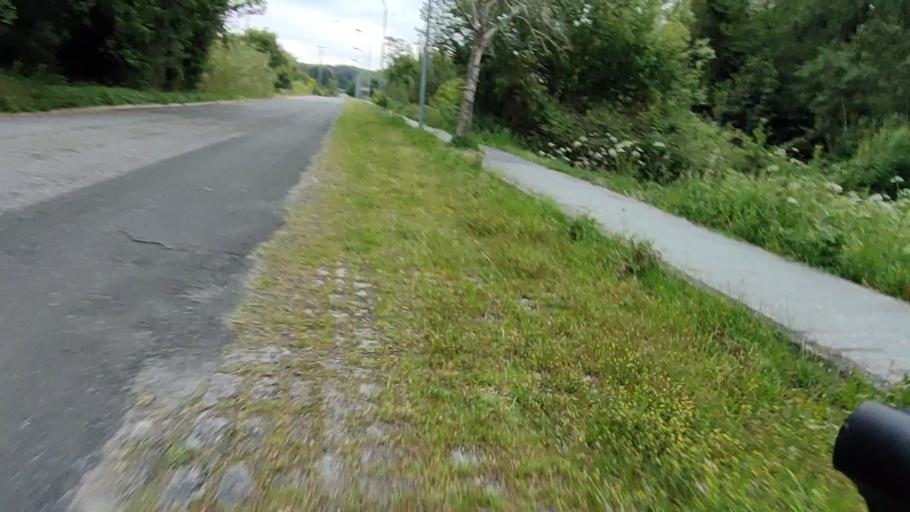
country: ES
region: Galicia
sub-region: Provincia da Coruna
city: Boiro
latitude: 42.6124
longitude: -8.8679
